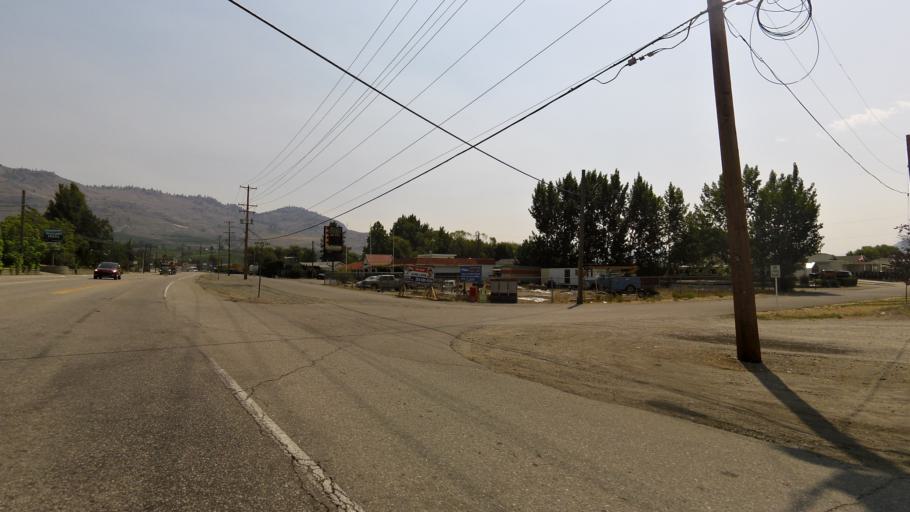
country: CA
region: British Columbia
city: Osoyoos
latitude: 49.0289
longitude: -119.4466
